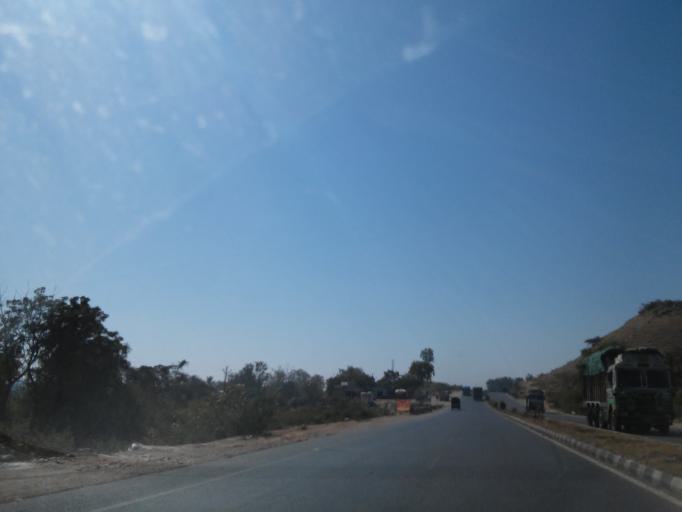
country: IN
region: Rajasthan
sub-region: Dungarpur
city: Dungarpur
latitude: 23.9253
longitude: 73.5665
